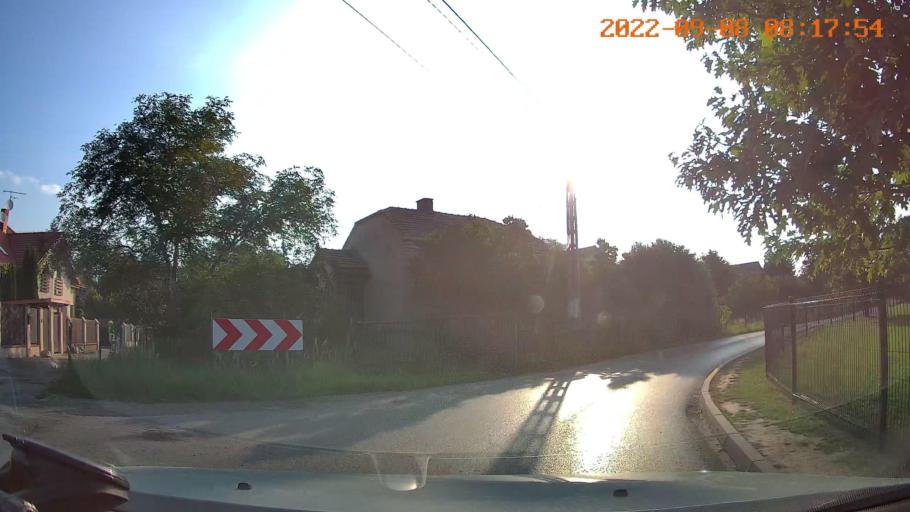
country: PL
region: Lesser Poland Voivodeship
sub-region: Powiat krakowski
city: Rzaska
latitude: 50.0709
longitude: 19.8837
